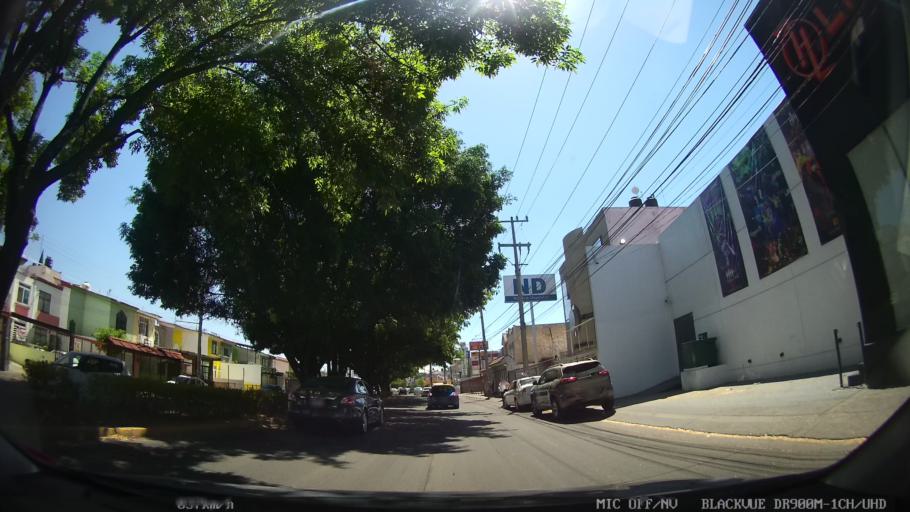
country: MX
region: Jalisco
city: Tlaquepaque
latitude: 20.6446
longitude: -103.2845
